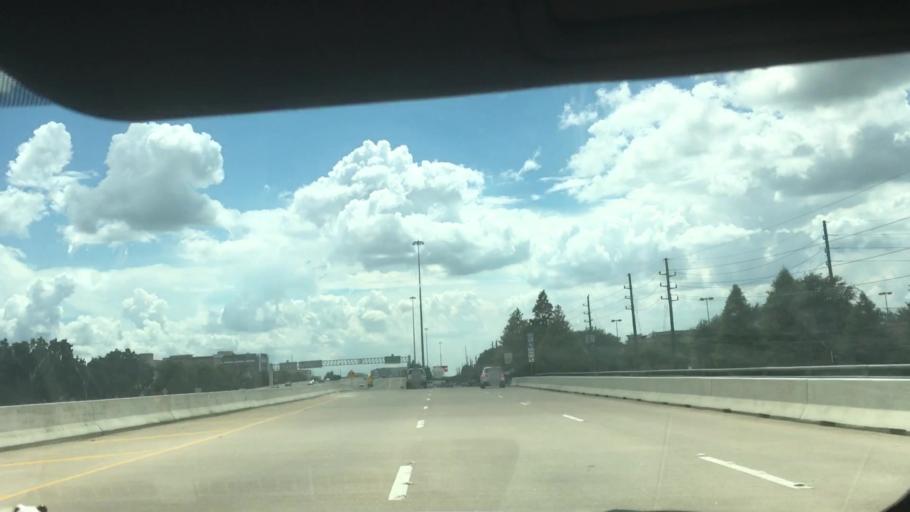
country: US
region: Texas
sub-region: Fort Bend County
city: Sugar Land
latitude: 29.6025
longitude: -95.6189
